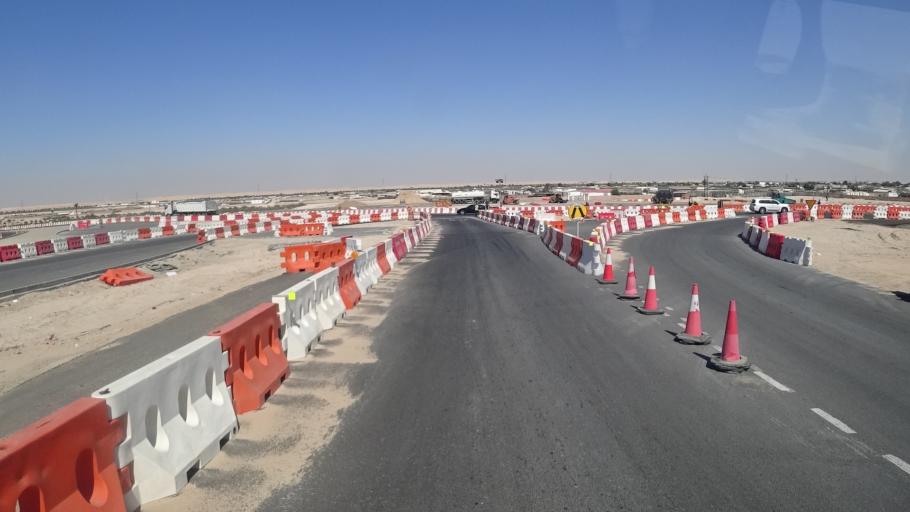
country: AE
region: Abu Dhabi
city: Abu Dhabi
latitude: 24.2010
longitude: 54.8577
